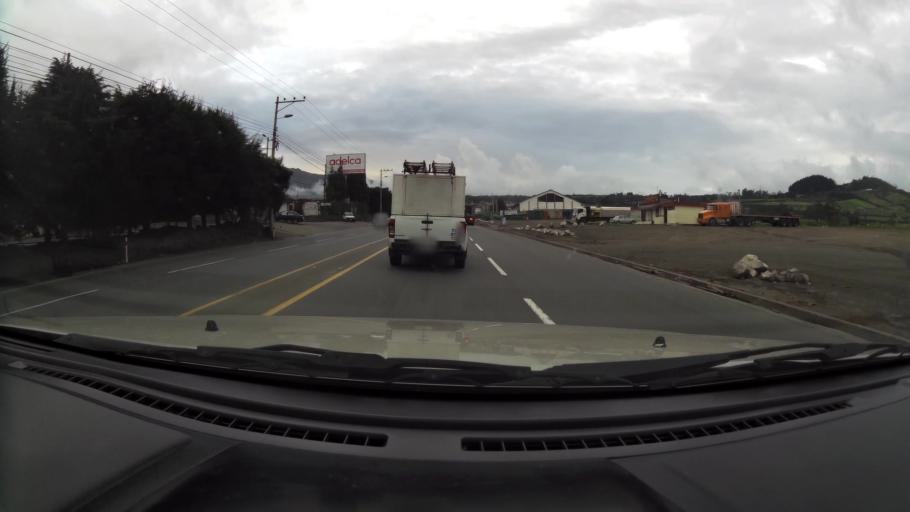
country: EC
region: Pichincha
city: Machachi
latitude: -0.4478
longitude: -78.6519
